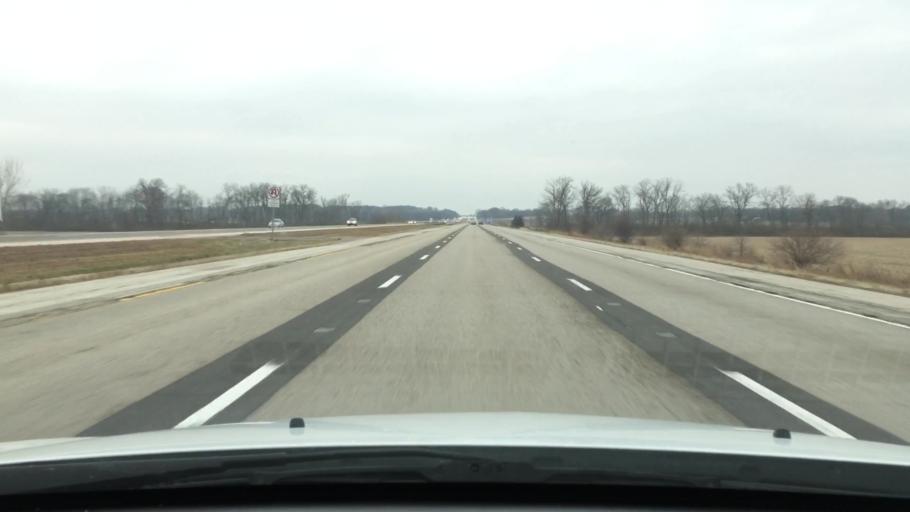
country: US
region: Illinois
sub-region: Logan County
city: Lincoln
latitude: 40.1240
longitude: -89.4166
